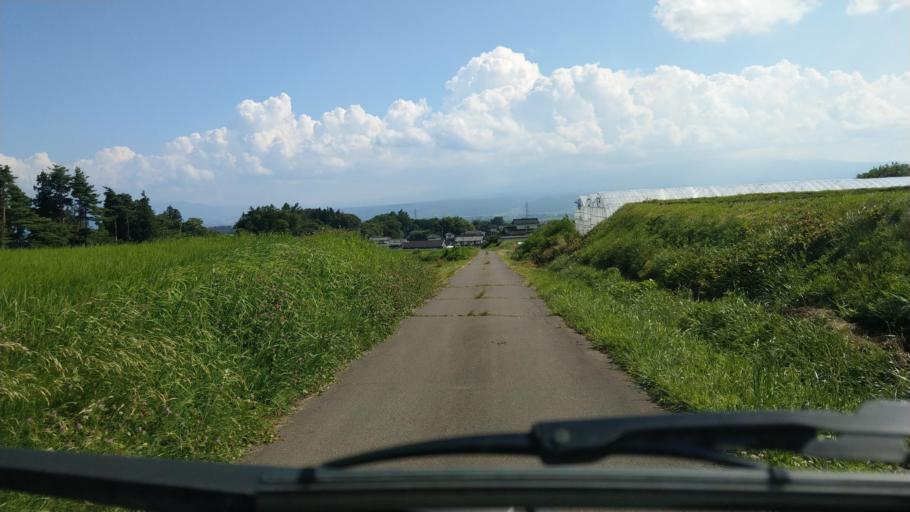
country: JP
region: Nagano
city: Komoro
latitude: 36.3256
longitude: 138.4501
